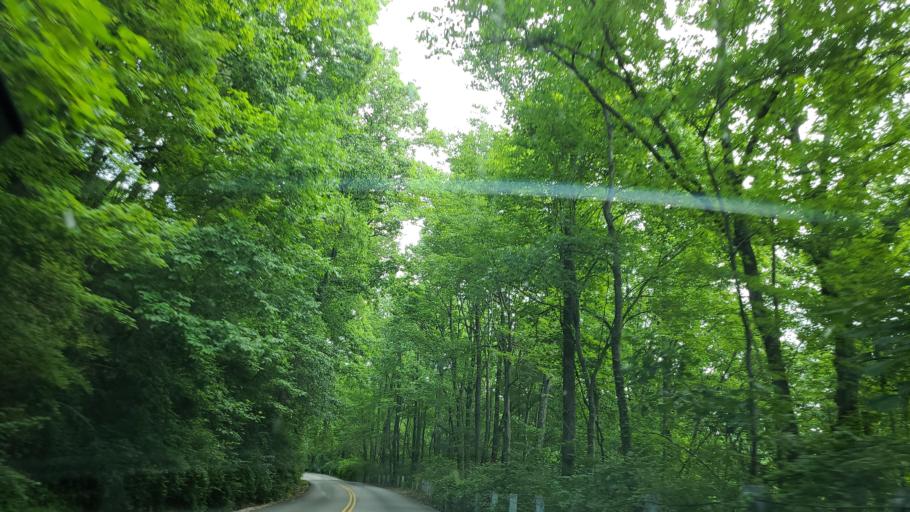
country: US
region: Tennessee
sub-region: Hamilton County
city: Lookout Mountain
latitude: 34.9892
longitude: -85.3472
